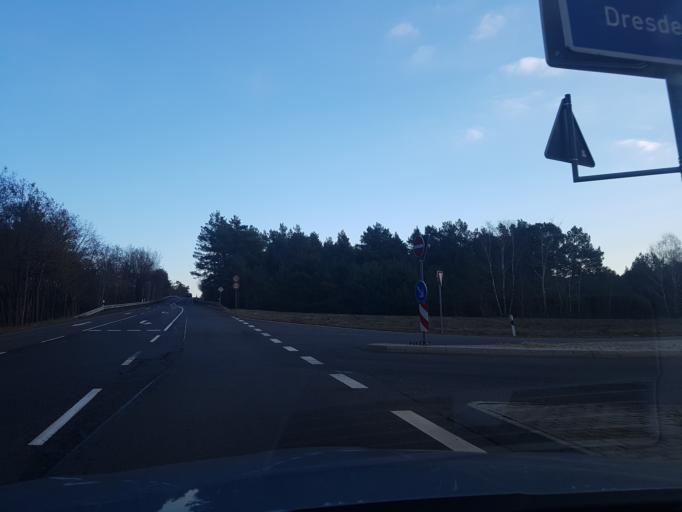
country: DE
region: Brandenburg
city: Kasel-Golzig
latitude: 52.0138
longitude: 13.6926
